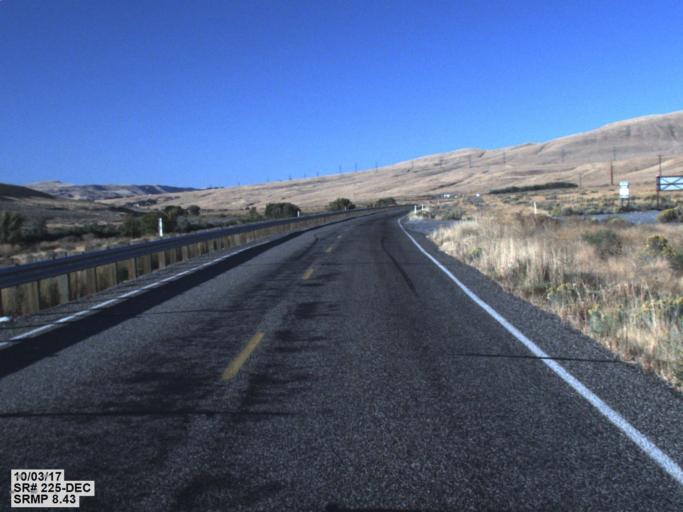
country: US
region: Washington
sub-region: Benton County
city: Benton City
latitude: 46.3543
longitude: -119.4564
